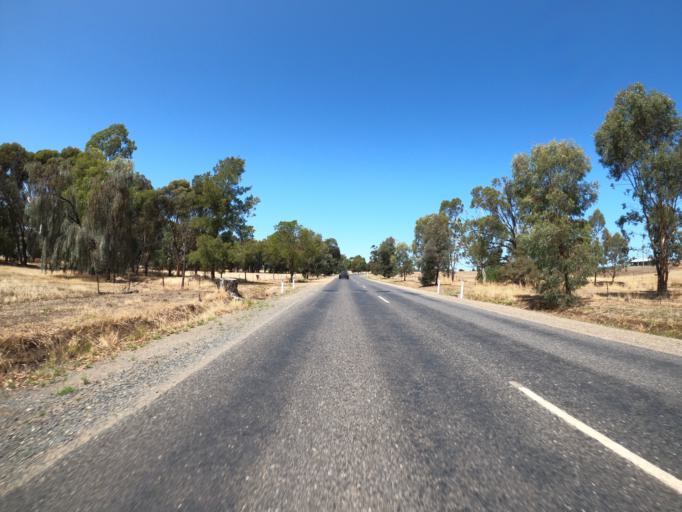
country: AU
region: New South Wales
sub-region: Corowa Shire
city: Corowa
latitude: -36.0135
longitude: 146.4074
